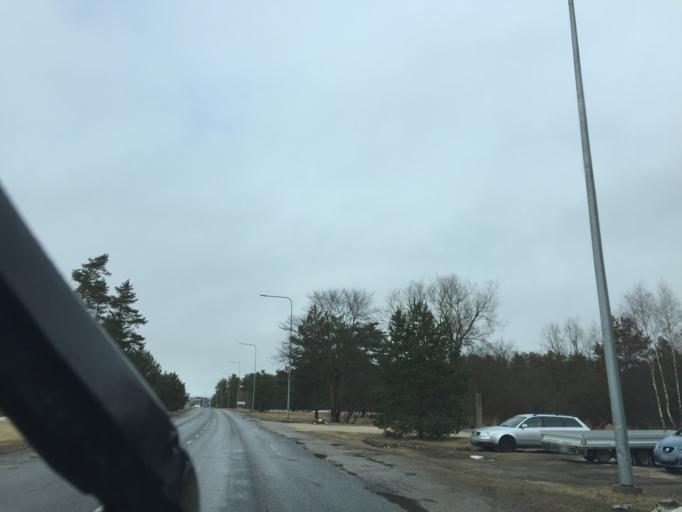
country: EE
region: Laeaene
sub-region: Haapsalu linn
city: Haapsalu
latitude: 58.9212
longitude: 23.5485
